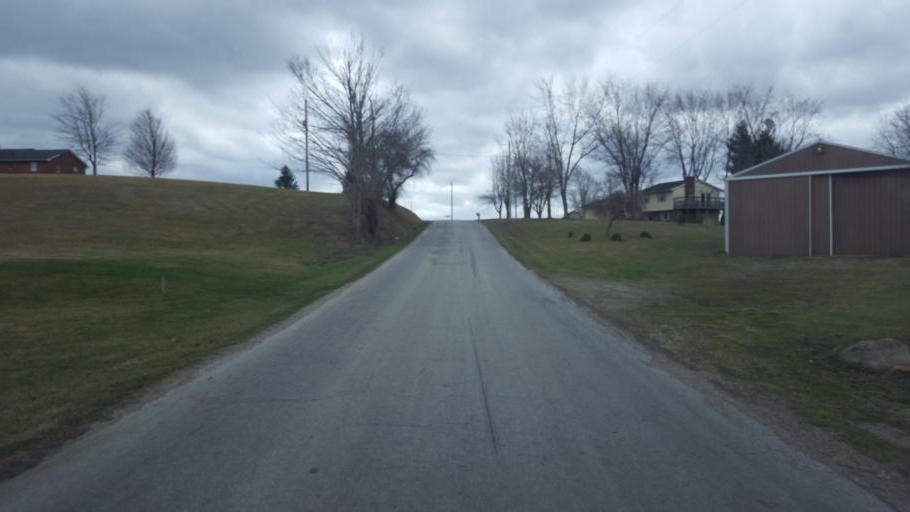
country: US
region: Ohio
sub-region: Licking County
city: Utica
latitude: 40.2443
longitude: -82.4123
